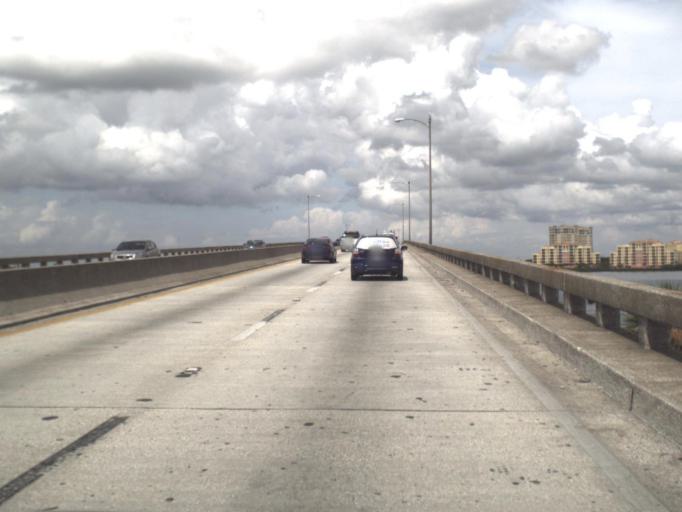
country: US
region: Florida
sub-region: Manatee County
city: Bradenton
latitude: 27.5008
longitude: -82.5630
